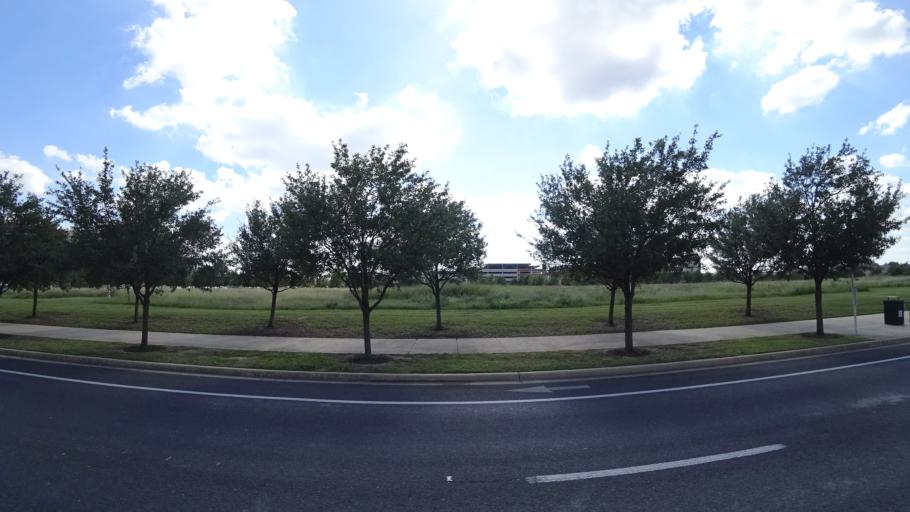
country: US
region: Texas
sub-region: Travis County
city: Austin
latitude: 30.3067
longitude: -97.7048
